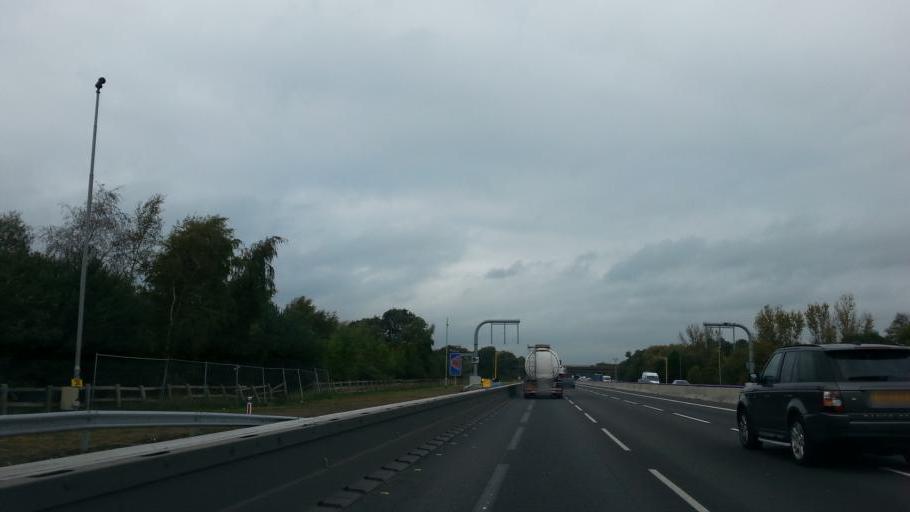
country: GB
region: England
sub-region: Cheshire East
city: Holmes Chapel
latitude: 53.2291
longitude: -2.3960
